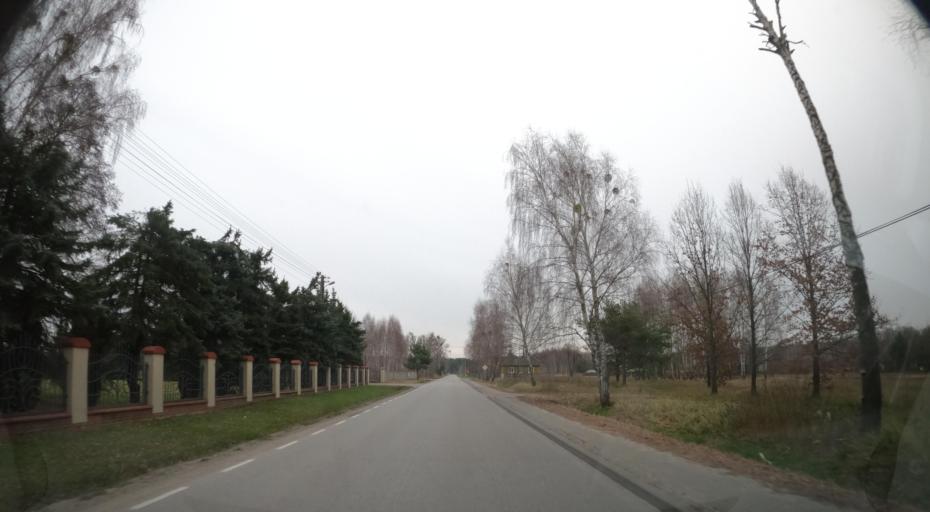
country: PL
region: Masovian Voivodeship
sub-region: Powiat radomski
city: Jedlinsk
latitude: 51.4907
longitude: 21.1386
